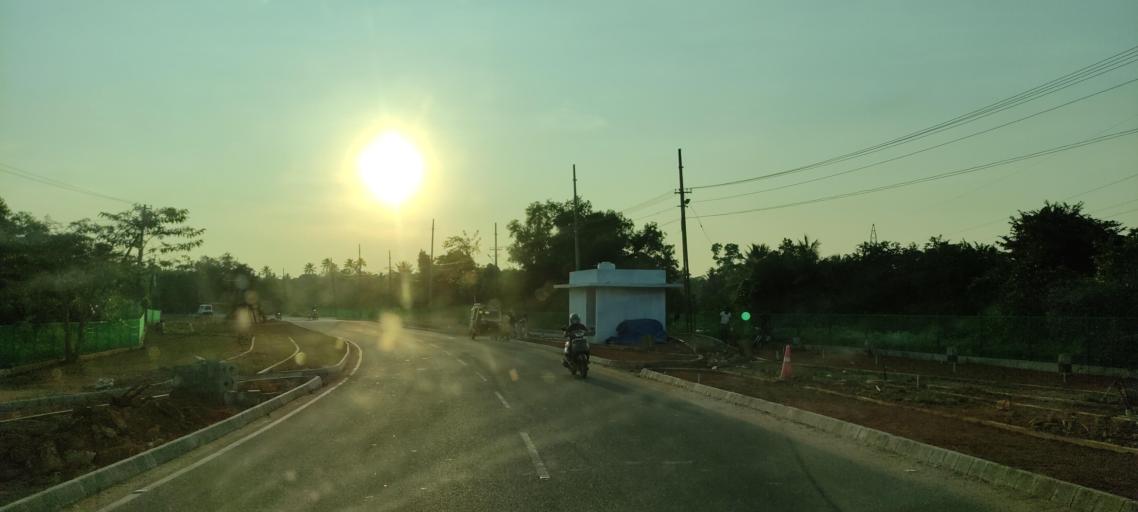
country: IN
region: Kerala
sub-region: Alappuzha
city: Kutiatodu
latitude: 9.7751
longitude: 76.3324
